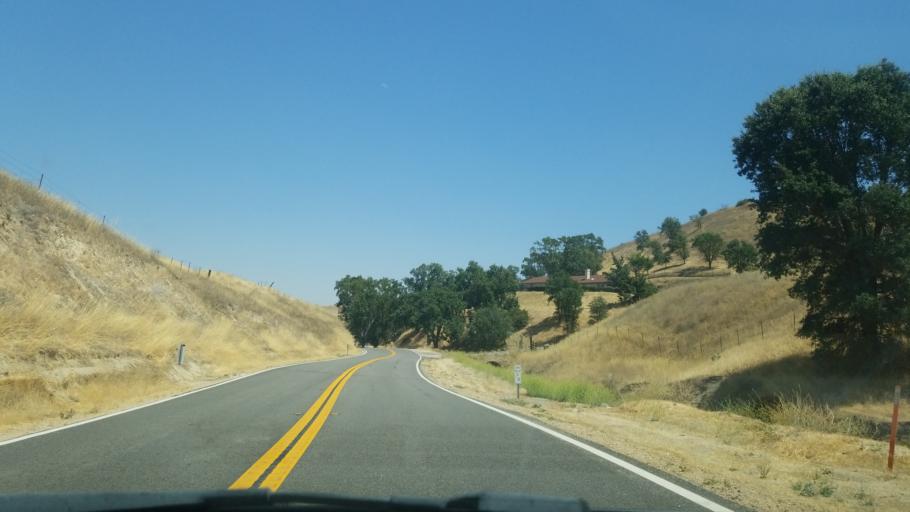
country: US
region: California
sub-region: San Luis Obispo County
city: Shandon
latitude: 35.5796
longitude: -120.4526
